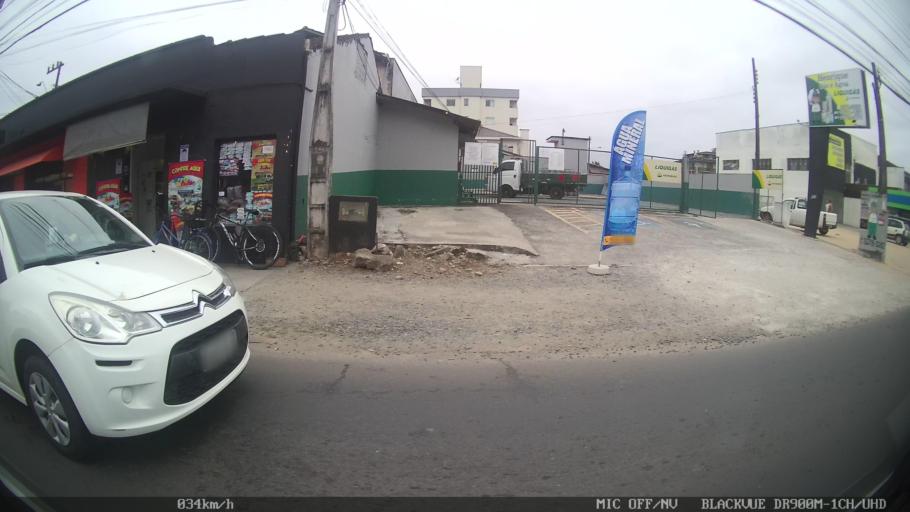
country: BR
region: Santa Catarina
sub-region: Joinville
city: Joinville
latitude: -26.3370
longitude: -48.8475
